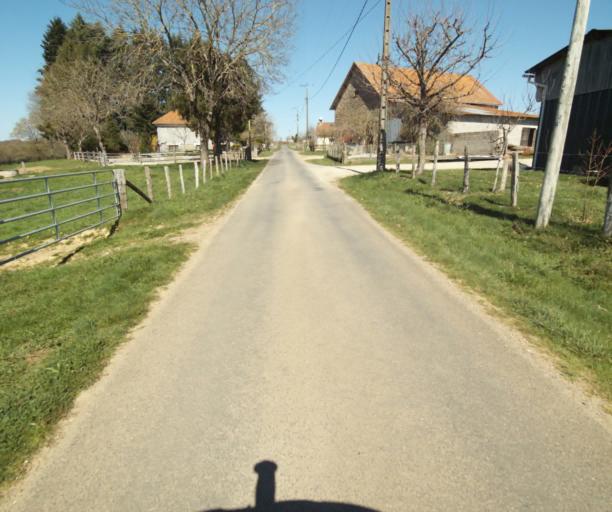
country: FR
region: Limousin
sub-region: Departement de la Correze
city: Saint-Clement
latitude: 45.3342
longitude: 1.7069
